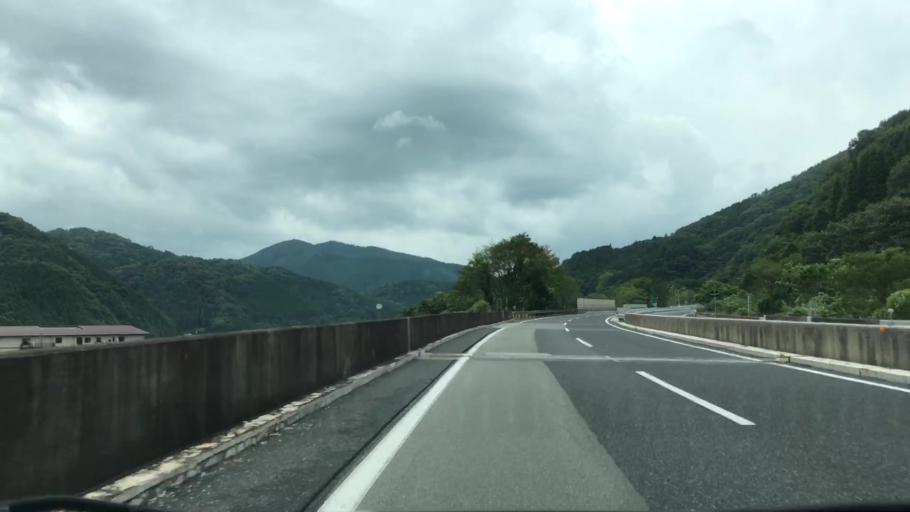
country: JP
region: Okayama
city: Niimi
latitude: 34.9992
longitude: 133.3991
